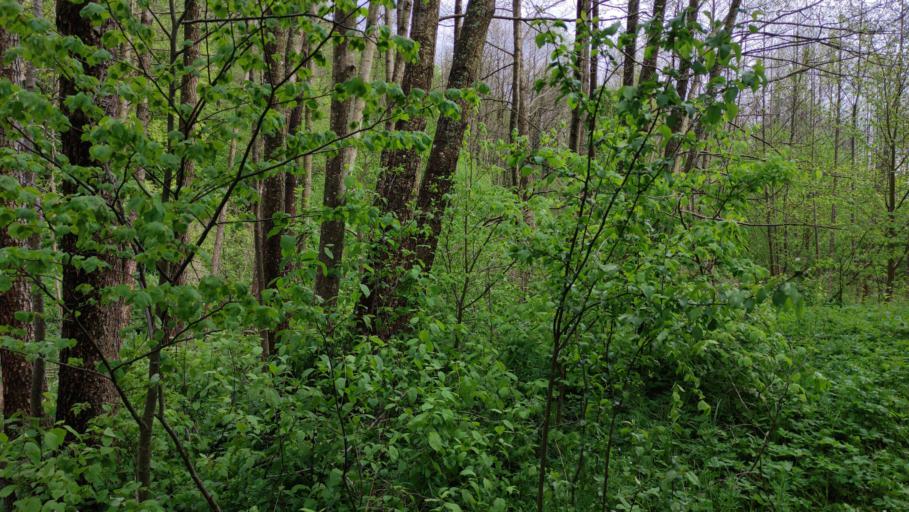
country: LT
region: Alytaus apskritis
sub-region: Alytus
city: Alytus
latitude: 54.4419
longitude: 24.0751
